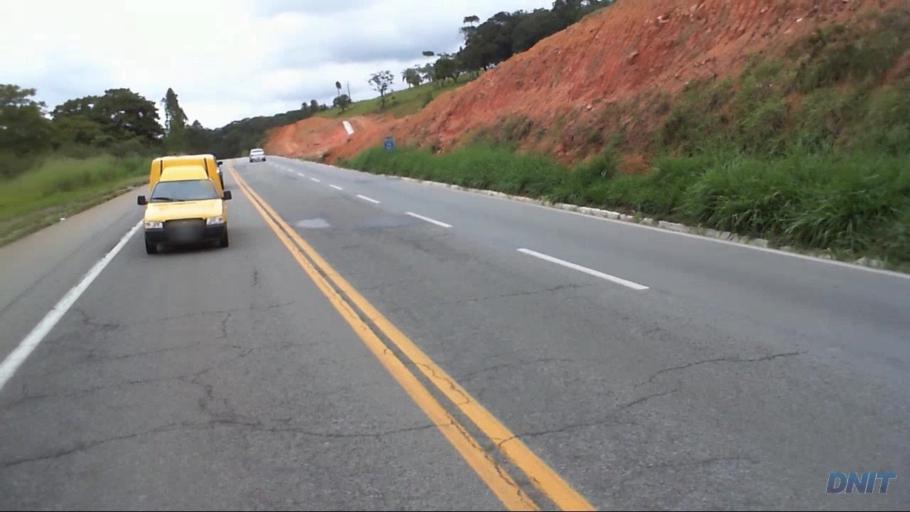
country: BR
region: Minas Gerais
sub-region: Barao De Cocais
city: Barao de Cocais
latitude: -19.7937
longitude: -43.4266
